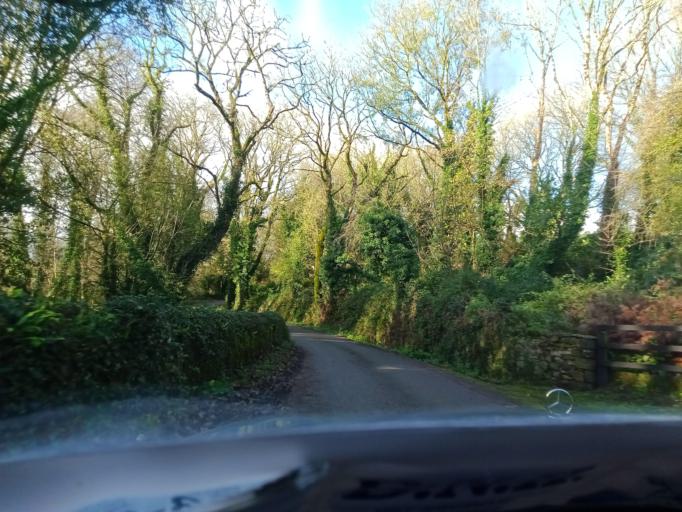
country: IE
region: Leinster
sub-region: Kilkenny
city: Mooncoin
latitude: 52.2759
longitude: -7.2439
